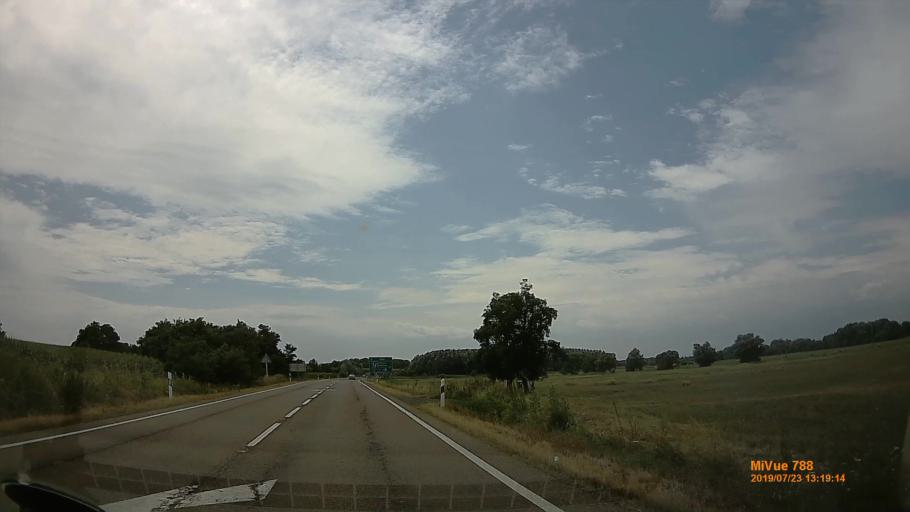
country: HU
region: Hajdu-Bihar
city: Polgar
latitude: 47.8758
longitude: 21.1426
